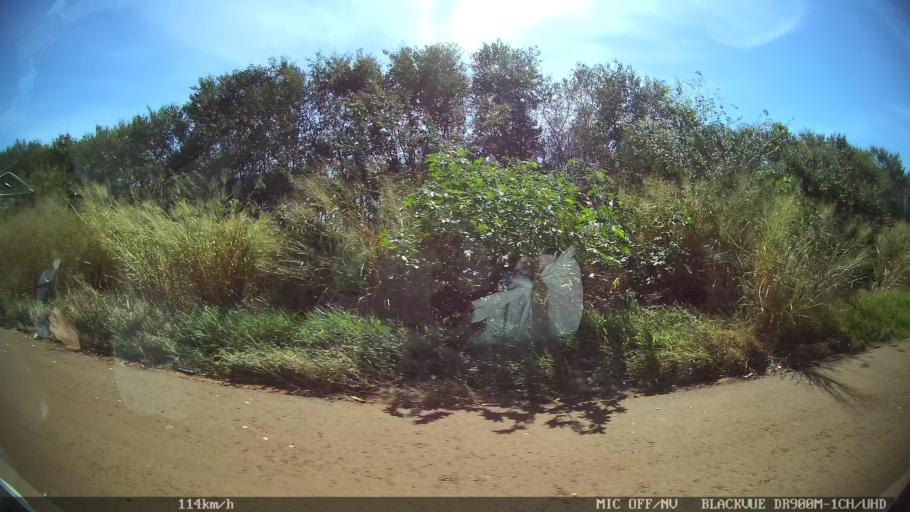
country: BR
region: Sao Paulo
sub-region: Franca
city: Franca
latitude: -20.5572
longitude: -47.5938
